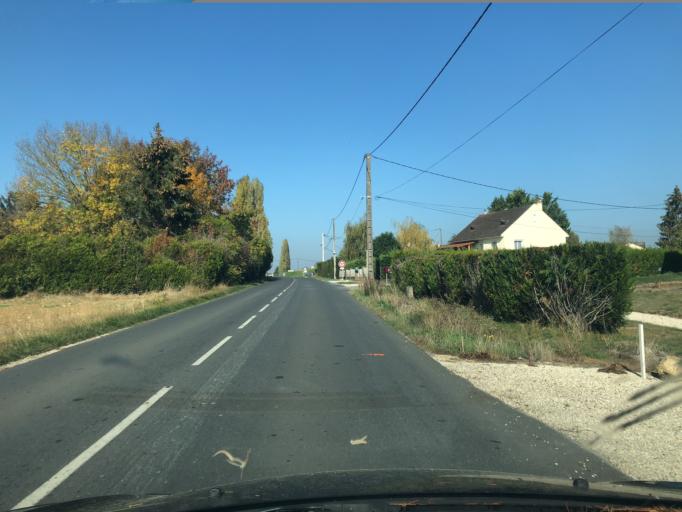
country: FR
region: Centre
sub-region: Departement d'Indre-et-Loire
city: Mettray
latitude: 47.4498
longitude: 0.6754
